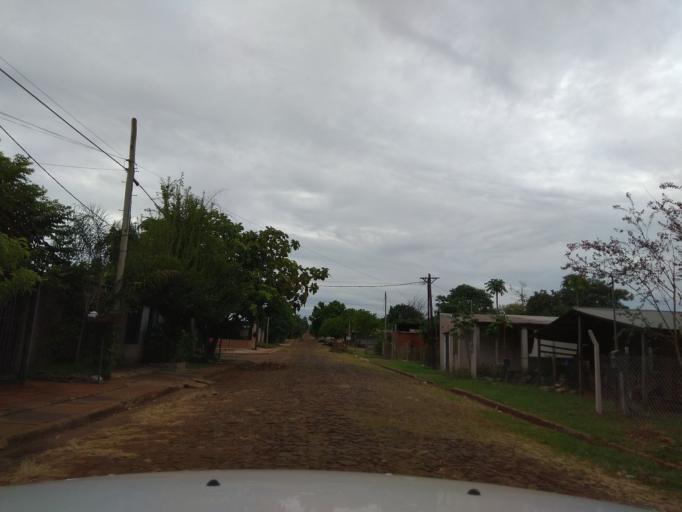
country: AR
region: Misiones
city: Garupa
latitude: -27.4447
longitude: -55.8522
